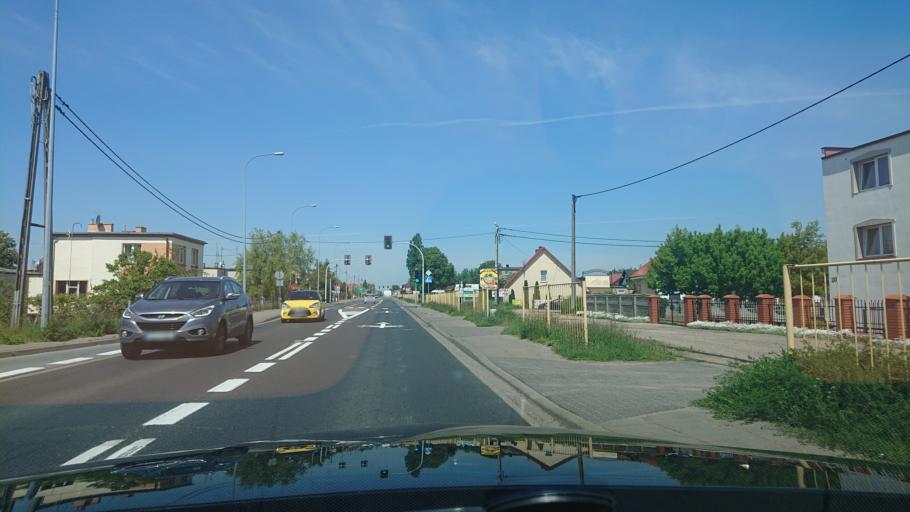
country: PL
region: Greater Poland Voivodeship
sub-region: Powiat gnieznienski
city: Gniezno
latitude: 52.5109
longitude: 17.6175
